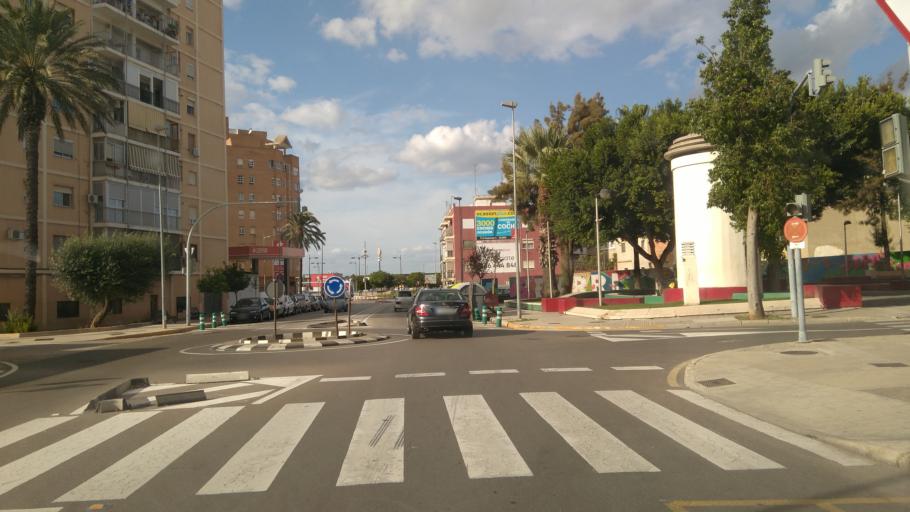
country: ES
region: Valencia
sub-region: Provincia de Valencia
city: Alzira
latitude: 39.1581
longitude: -0.4290
